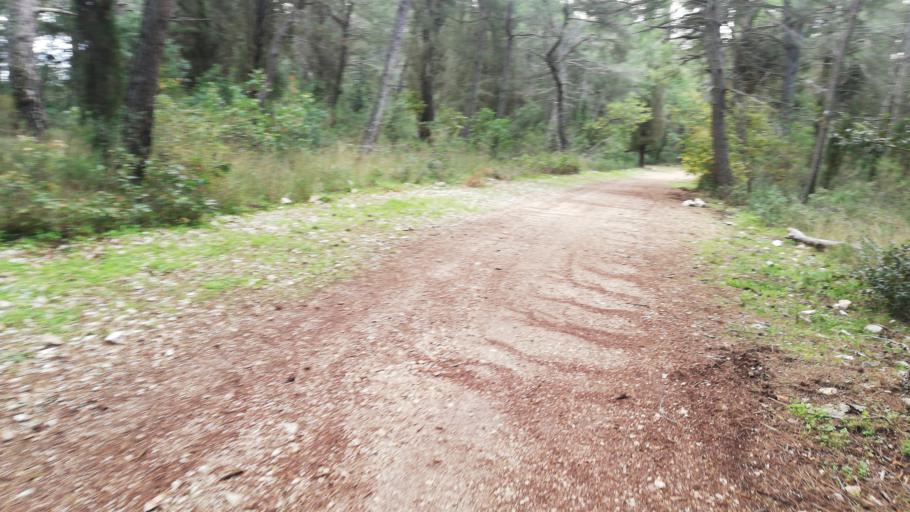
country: IT
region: Apulia
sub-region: Provincia di Bari
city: Cassano delle Murge
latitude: 40.8726
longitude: 16.7142
